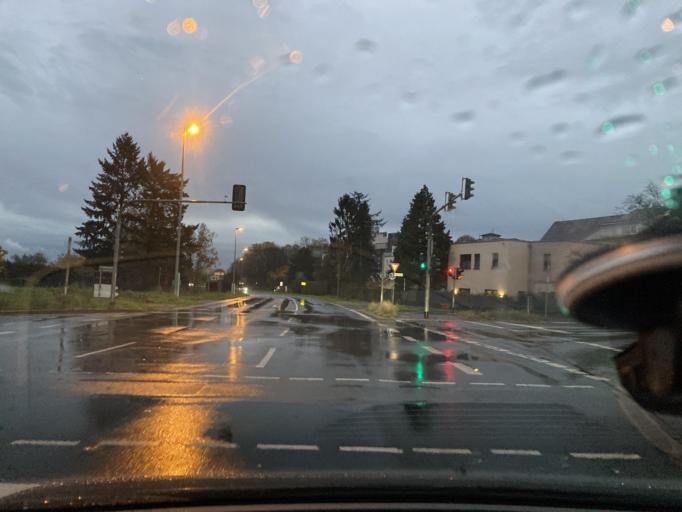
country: DE
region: Hesse
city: Kelkheim (Taunus)
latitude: 50.1253
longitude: 8.4669
